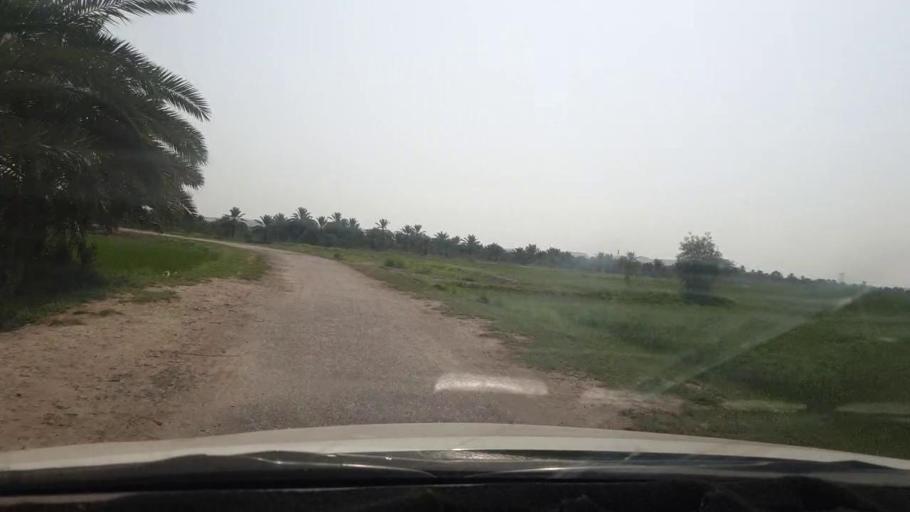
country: PK
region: Sindh
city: Rohri
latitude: 27.6111
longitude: 68.8951
